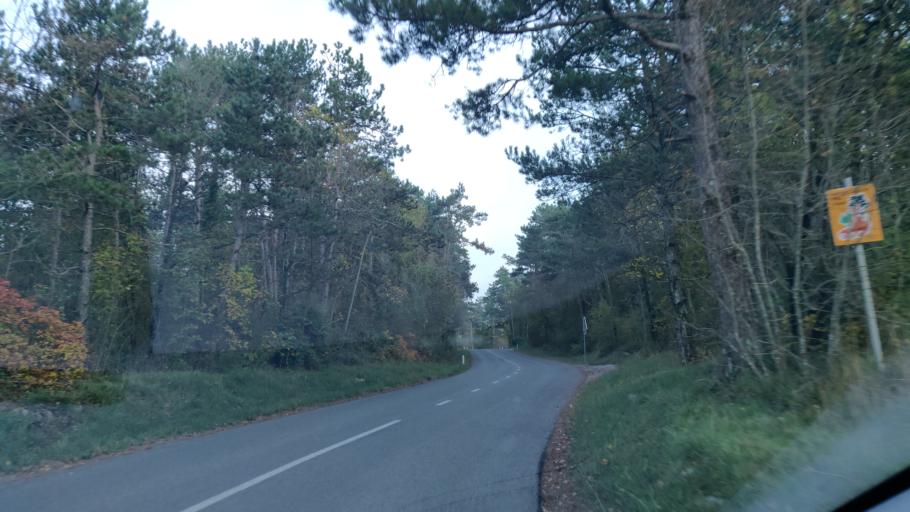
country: IT
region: Friuli Venezia Giulia
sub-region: Provincia di Trieste
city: Zolla
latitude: 45.8052
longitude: 13.8455
